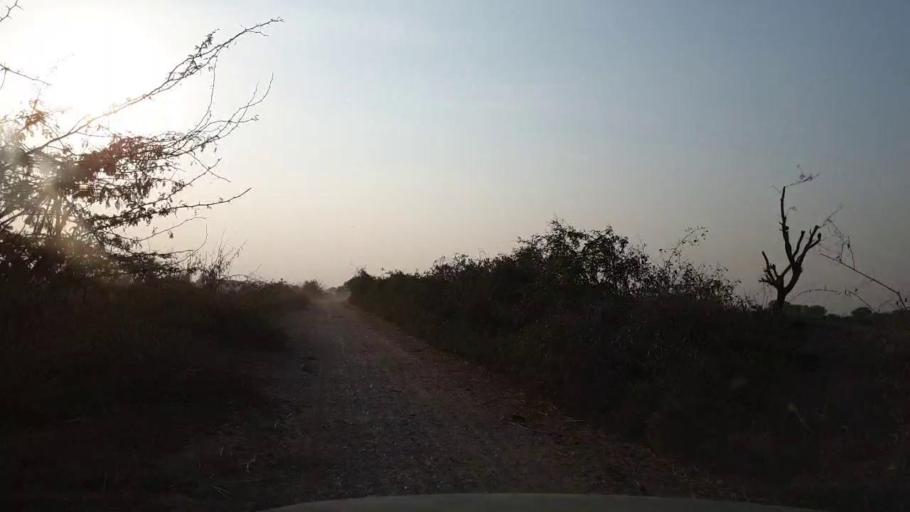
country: PK
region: Sindh
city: Pithoro
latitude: 25.6537
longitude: 69.2138
